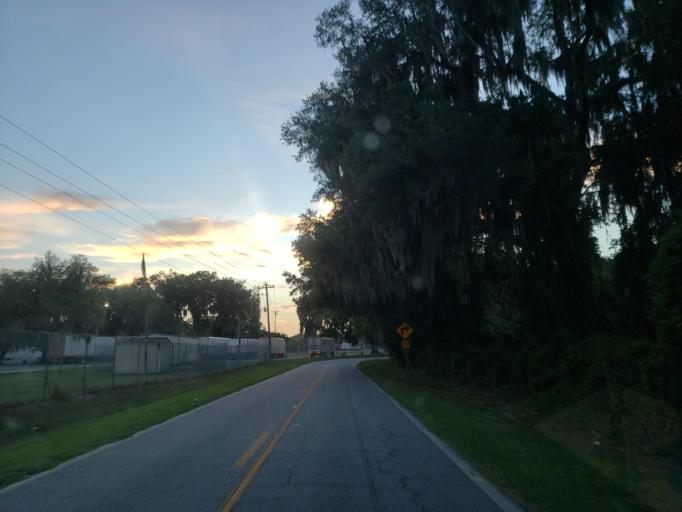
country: US
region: Georgia
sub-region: Echols County
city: Statenville
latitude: 30.6639
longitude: -83.2065
